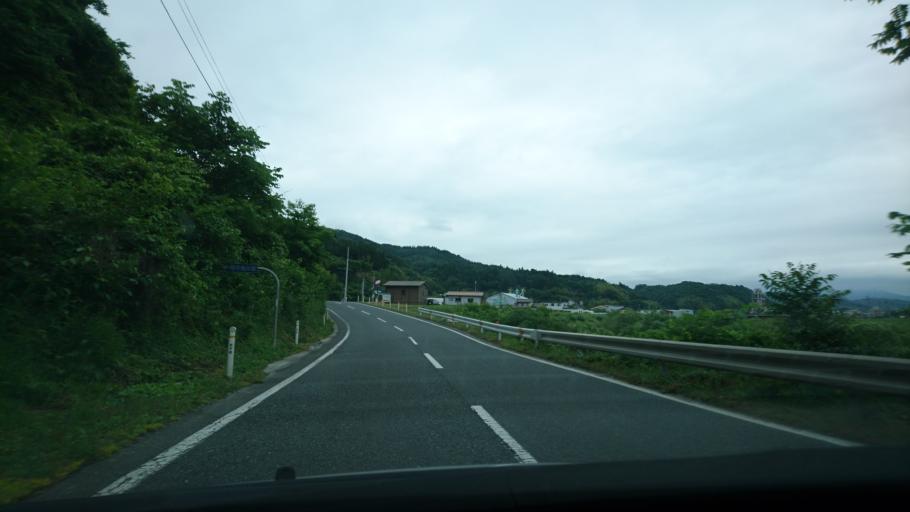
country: JP
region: Iwate
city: Ichinoseki
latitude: 38.9729
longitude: 141.2382
